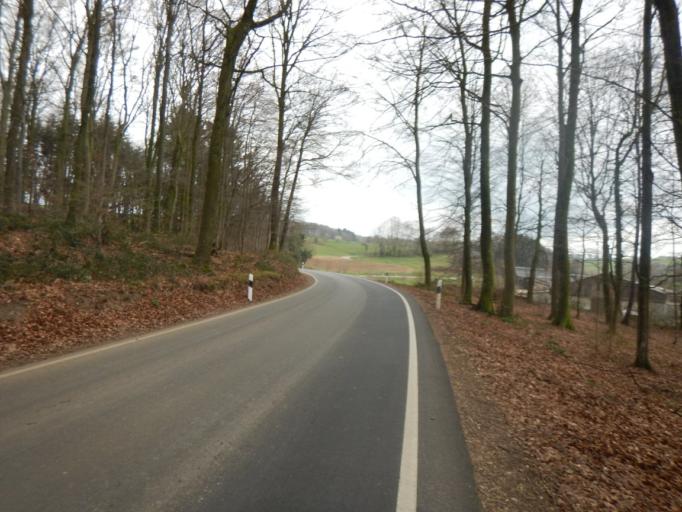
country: LU
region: Diekirch
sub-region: Canton de Redange
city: Ell
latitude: 49.7862
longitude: 5.8449
